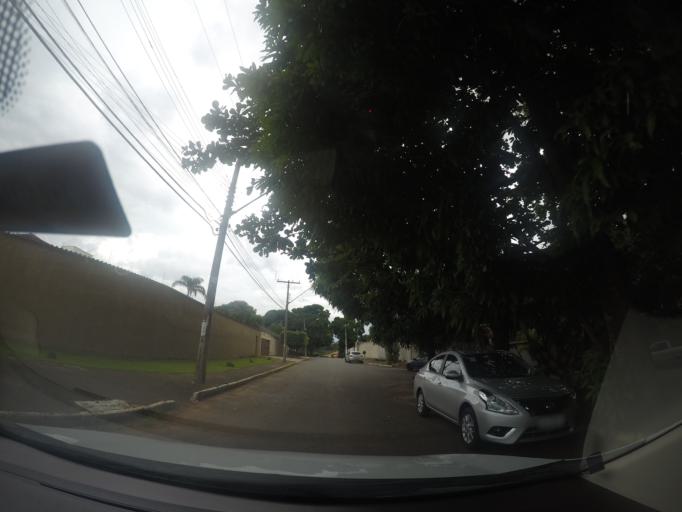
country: BR
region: Goias
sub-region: Goiania
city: Goiania
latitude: -16.6533
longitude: -49.2297
